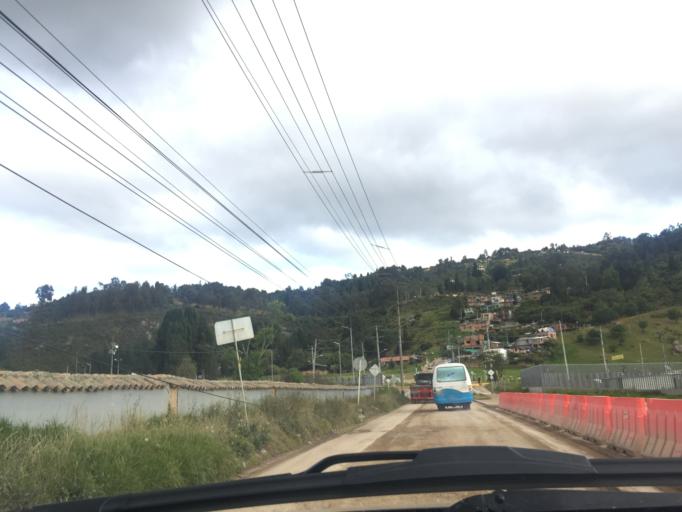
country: CO
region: Cundinamarca
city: Sopo
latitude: 4.9340
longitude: -73.9359
